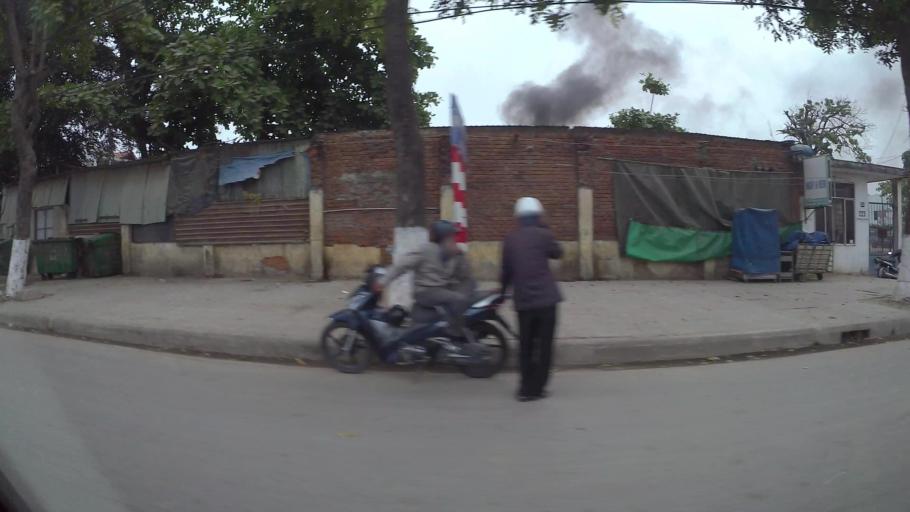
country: VN
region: Da Nang
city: Thanh Khe
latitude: 16.0530
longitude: 108.1818
